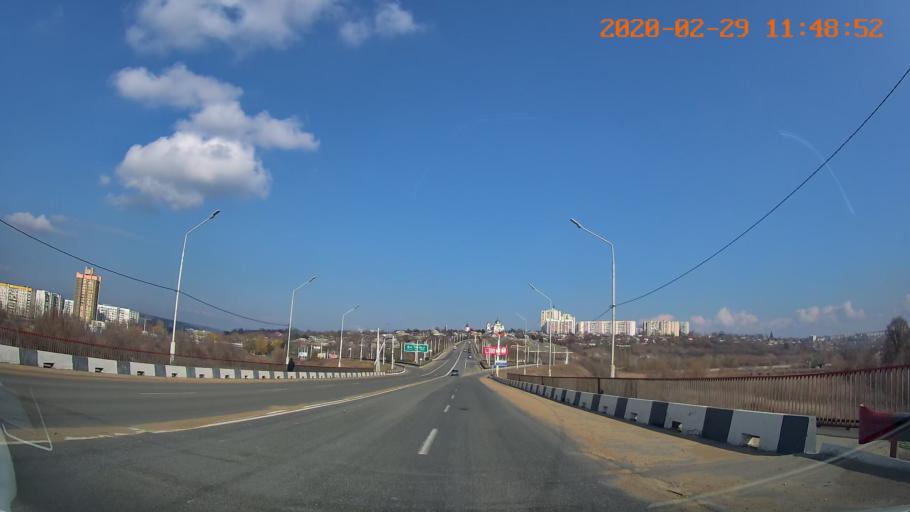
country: MD
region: Telenesti
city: Ribnita
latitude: 47.7509
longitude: 28.9928
